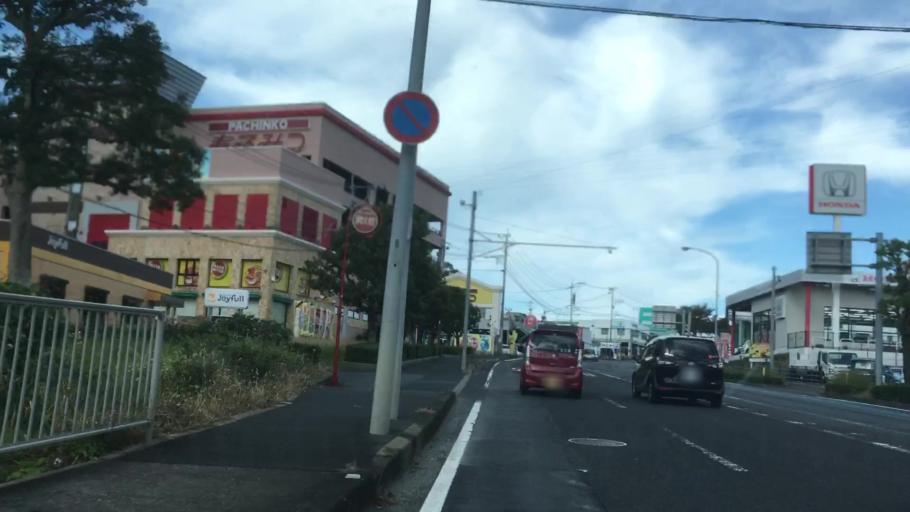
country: JP
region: Nagasaki
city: Sasebo
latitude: 33.1563
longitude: 129.7688
